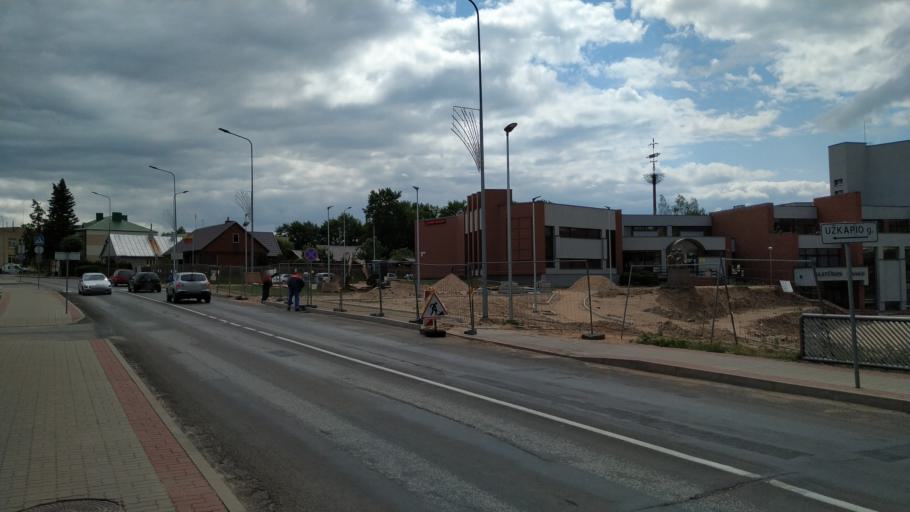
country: LT
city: Kupiskis
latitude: 55.8373
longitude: 24.9770
